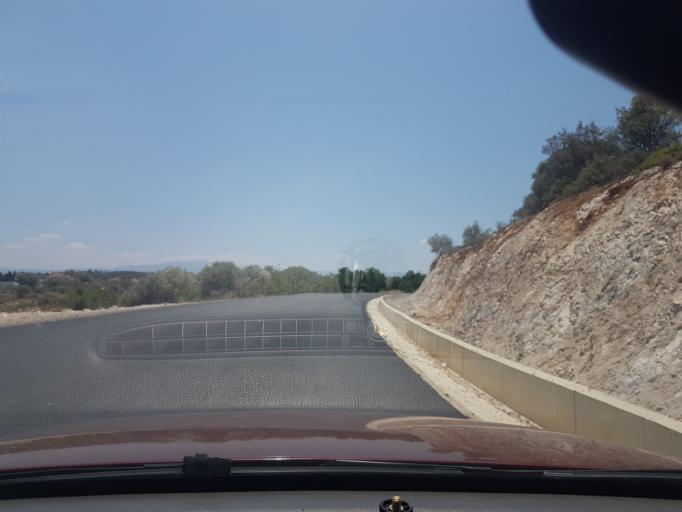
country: GR
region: Central Greece
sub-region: Nomos Evvoias
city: Filla
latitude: 38.4451
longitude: 23.6732
